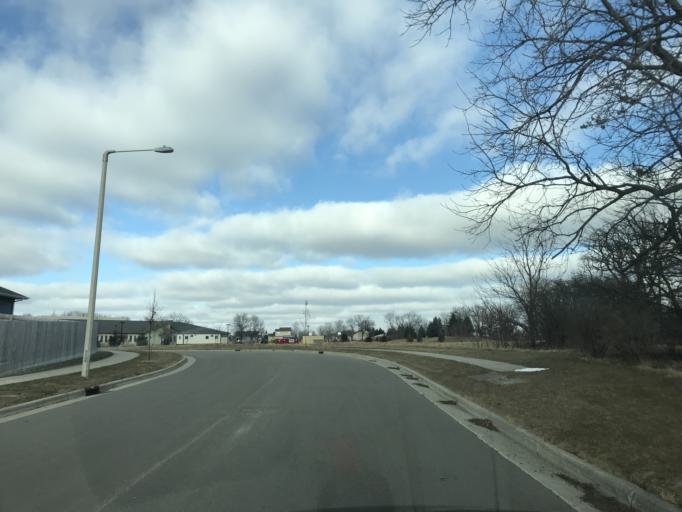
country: US
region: Wisconsin
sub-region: Dane County
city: Monona
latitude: 43.1076
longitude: -89.2869
